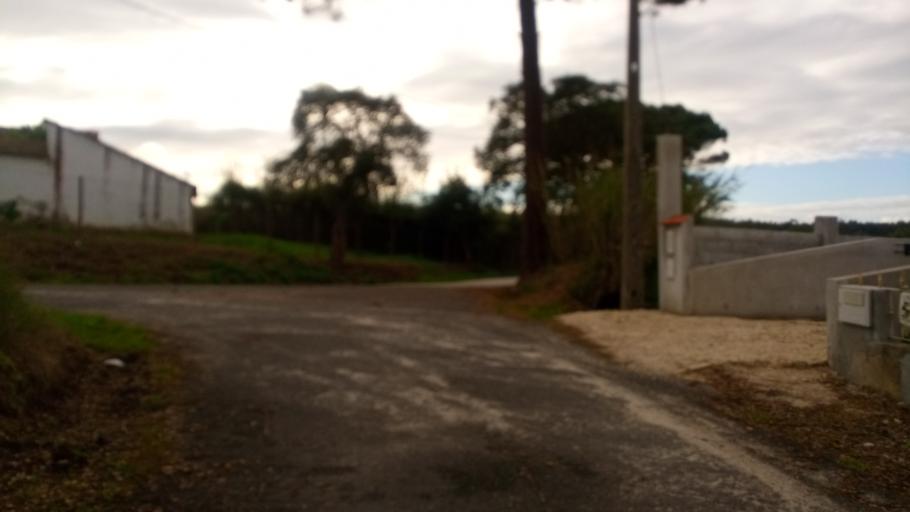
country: PT
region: Leiria
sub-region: Caldas da Rainha
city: Caldas da Rainha
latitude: 39.4525
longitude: -9.1712
